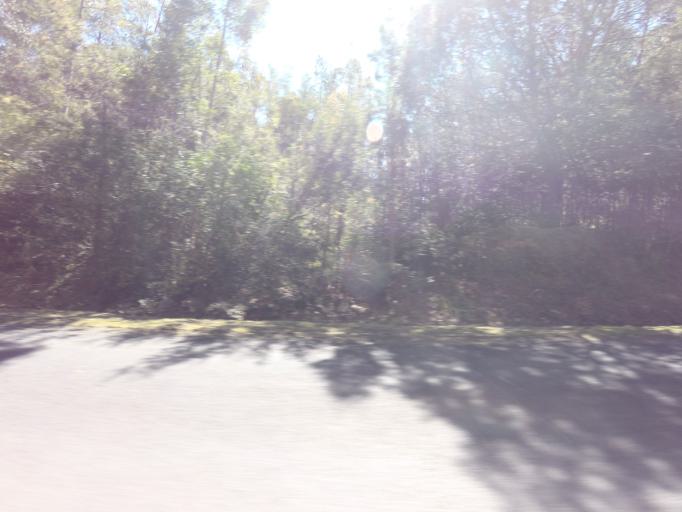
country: AU
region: Tasmania
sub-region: Huon Valley
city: Geeveston
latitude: -42.8175
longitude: 146.3548
